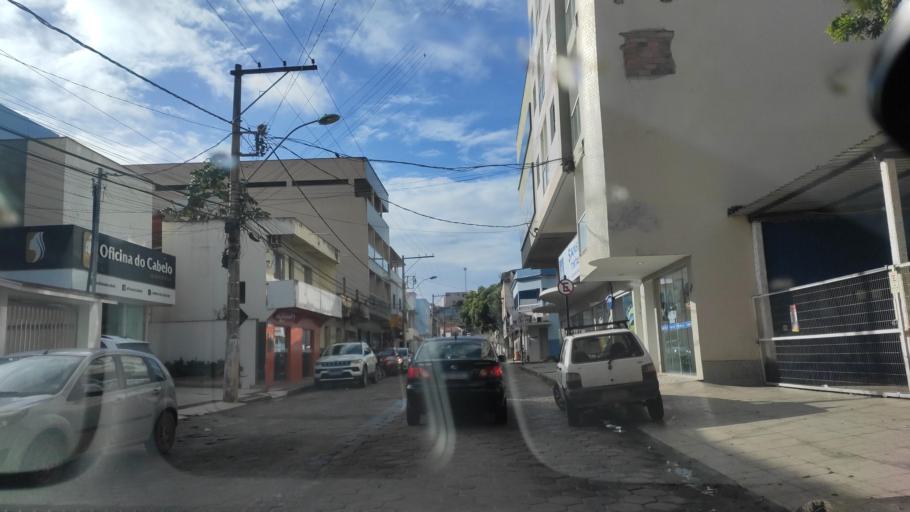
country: BR
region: Espirito Santo
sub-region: Nova Venecia
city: Nova Venecia
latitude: -18.7129
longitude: -40.3956
